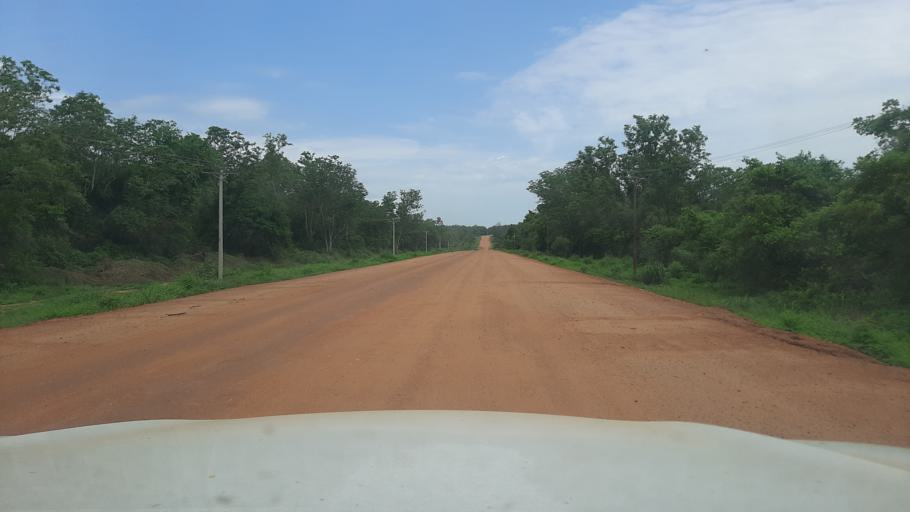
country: ET
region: Gambela
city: Gambela
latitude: 8.0947
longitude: 34.5883
